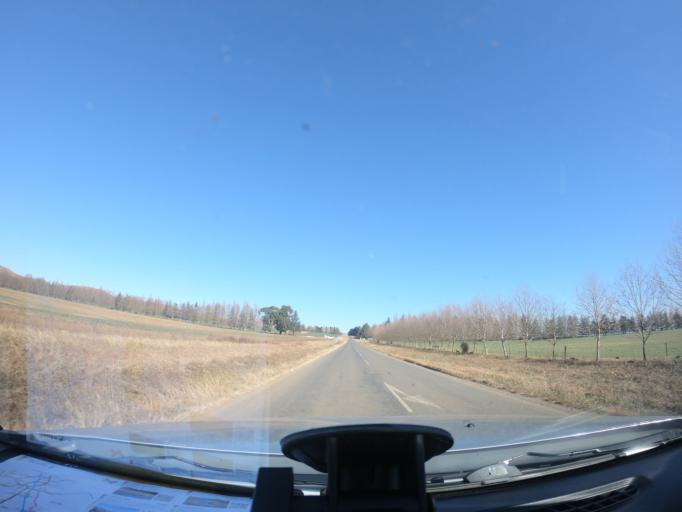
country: ZA
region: KwaZulu-Natal
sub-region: uMgungundlovu District Municipality
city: Mooirivier
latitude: -29.3259
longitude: 29.8301
